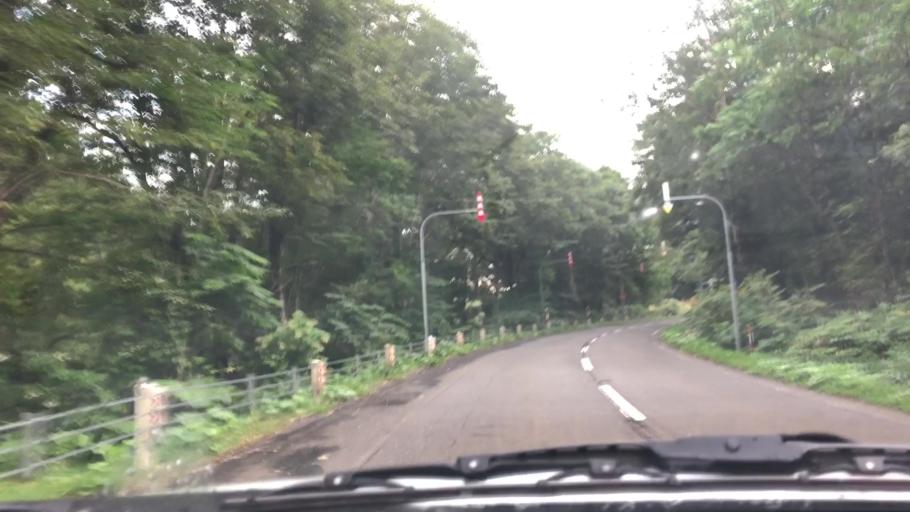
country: JP
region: Hokkaido
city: Shimo-furano
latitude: 42.9120
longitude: 142.3725
